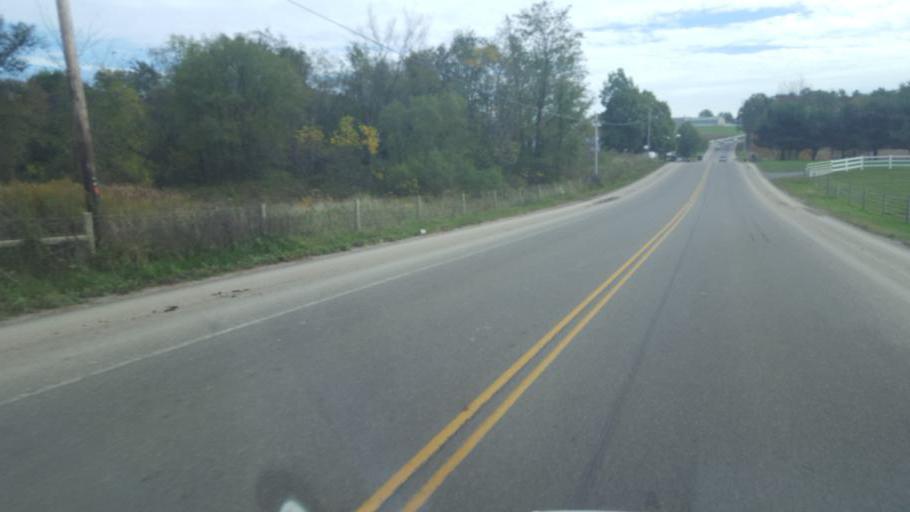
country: US
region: Ohio
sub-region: Wayne County
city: Apple Creek
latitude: 40.6153
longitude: -81.7823
